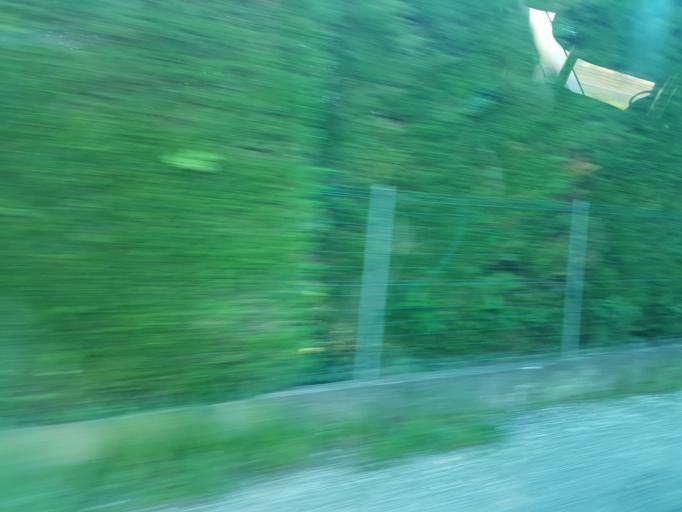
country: IT
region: Veneto
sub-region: Provincia di Padova
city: Cadoneghe
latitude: 45.4317
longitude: 11.9339
